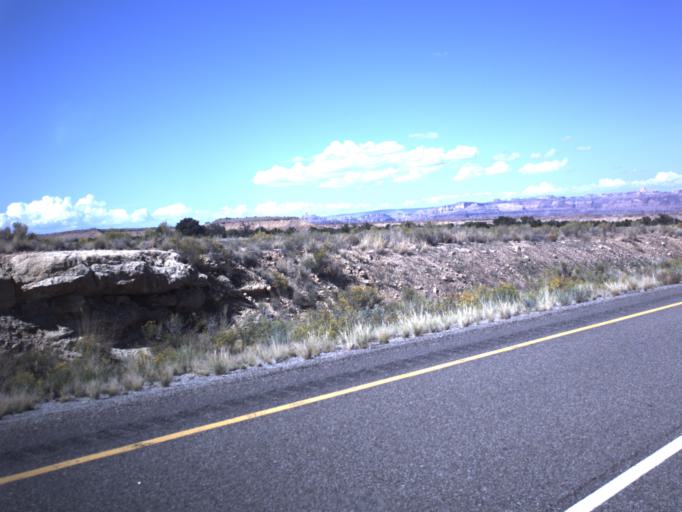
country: US
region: Utah
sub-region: Emery County
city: Castle Dale
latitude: 38.9194
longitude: -110.5011
